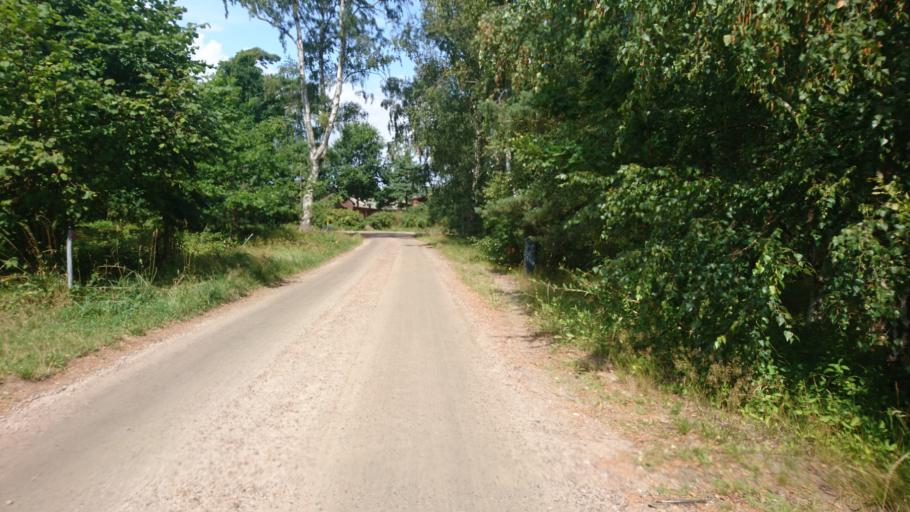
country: SE
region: Skane
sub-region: Vellinge Kommun
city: Ljunghusen
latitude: 55.3923
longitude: 12.9113
